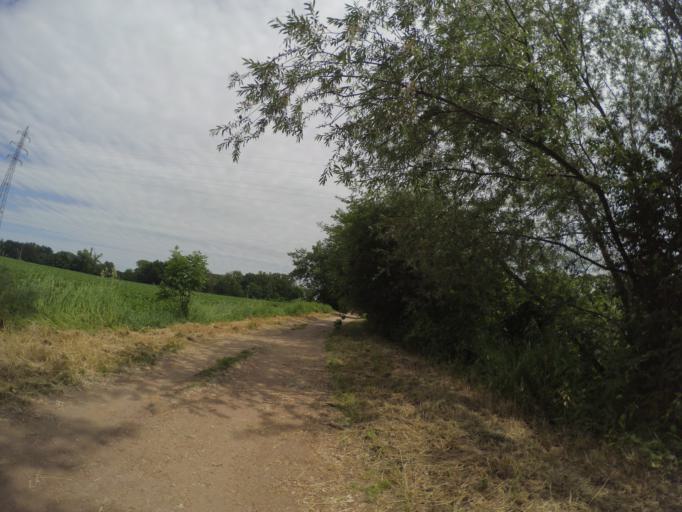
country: CZ
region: Central Bohemia
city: Prerov nad Labem
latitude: 50.1727
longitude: 14.8655
